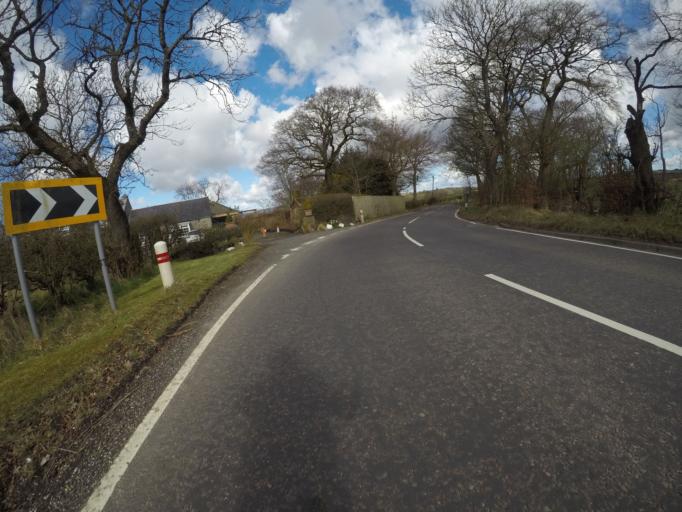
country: GB
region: Scotland
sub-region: North Ayrshire
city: Beith
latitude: 55.7375
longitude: -4.6204
